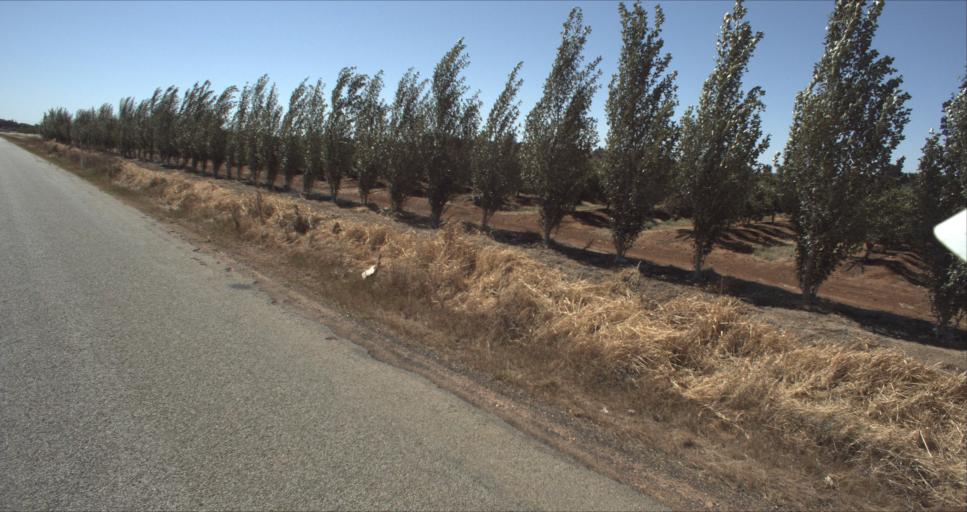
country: AU
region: New South Wales
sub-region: Leeton
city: Leeton
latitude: -34.5455
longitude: 146.3679
